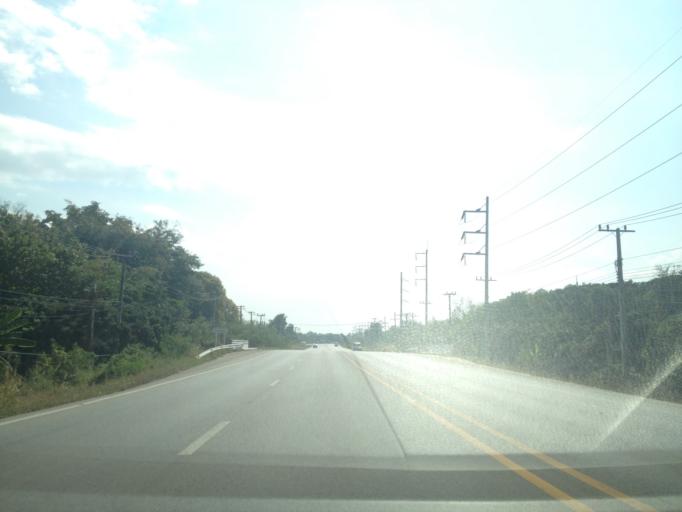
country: TH
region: Chiang Mai
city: Hot
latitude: 18.2248
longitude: 98.6132
